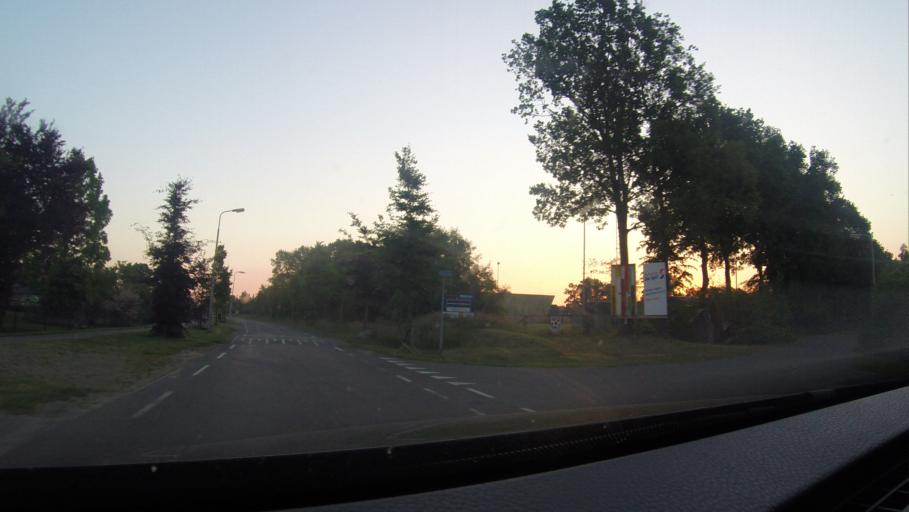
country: NL
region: Gelderland
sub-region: Gemeente Lochem
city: Harfsen
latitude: 52.2792
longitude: 6.2725
